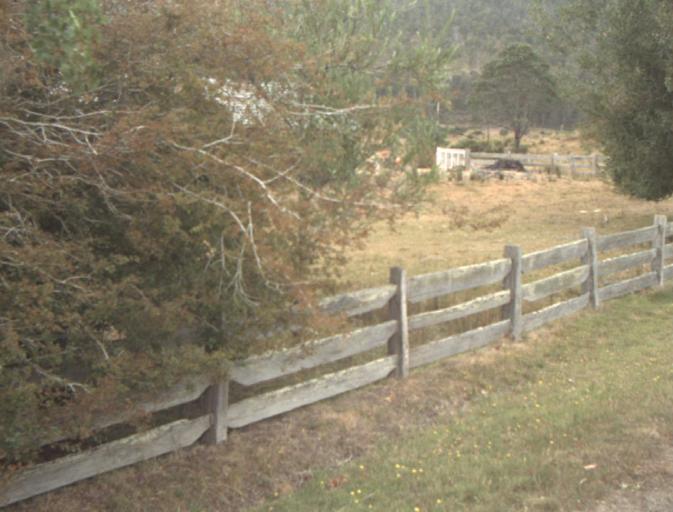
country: AU
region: Tasmania
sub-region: Northern Midlands
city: Evandale
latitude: -41.4873
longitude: 147.4384
